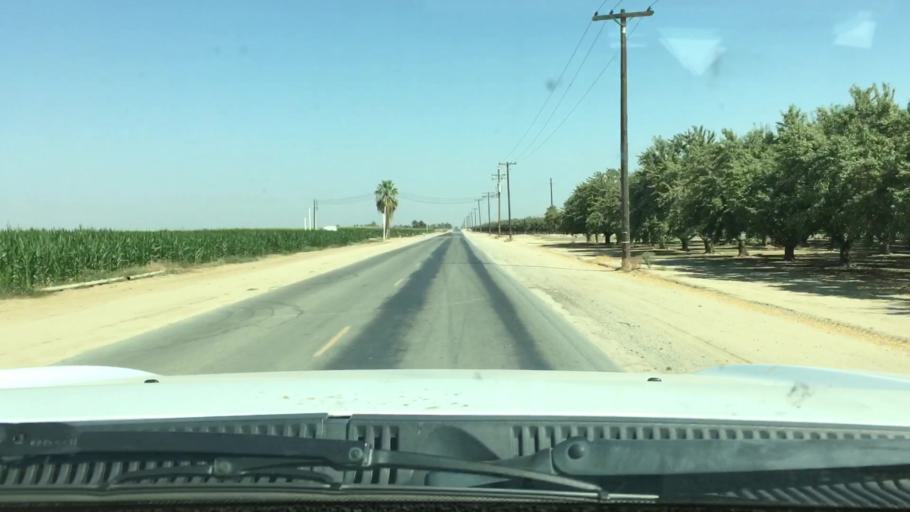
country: US
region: California
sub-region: Kern County
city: Wasco
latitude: 35.6720
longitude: -119.4374
